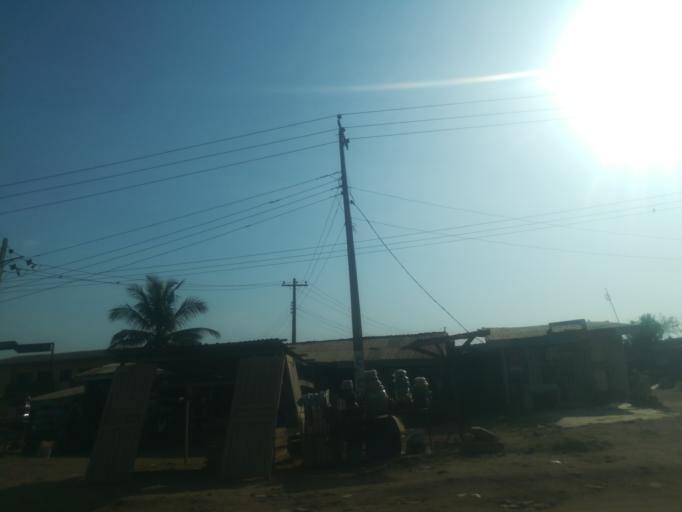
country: NG
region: Ogun
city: Abeokuta
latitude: 7.1801
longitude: 3.2834
